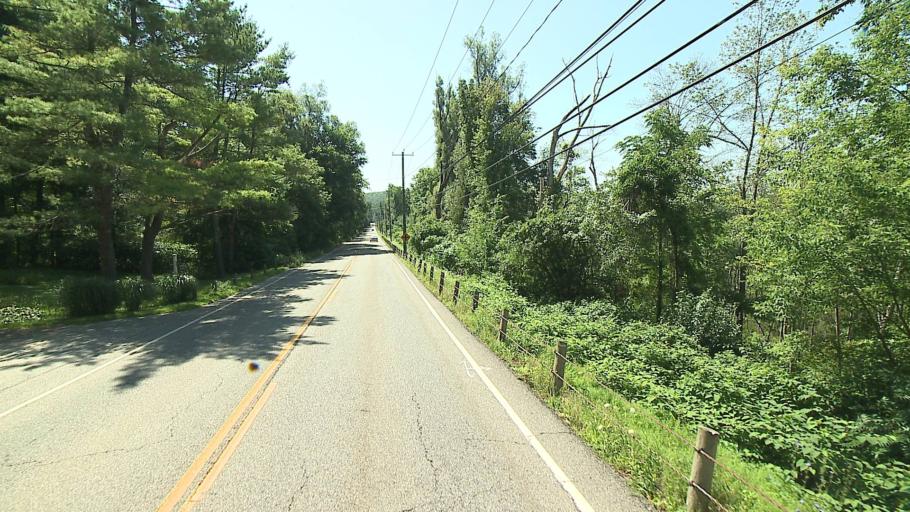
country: US
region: Connecticut
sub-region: Litchfield County
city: Kent
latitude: 41.8684
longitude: -73.4642
